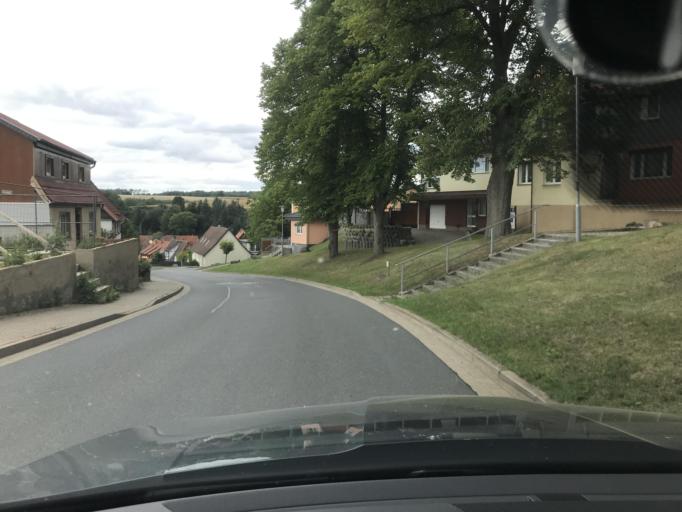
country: DE
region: Saxony-Anhalt
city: Friedrichsbrunn
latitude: 51.6151
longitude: 11.0487
